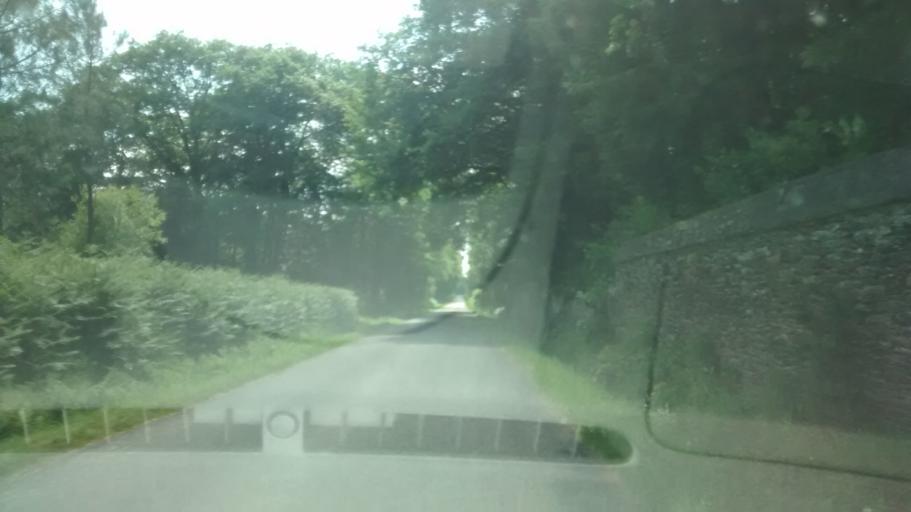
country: FR
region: Brittany
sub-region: Departement du Morbihan
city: Augan
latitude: 47.8833
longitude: -2.2395
